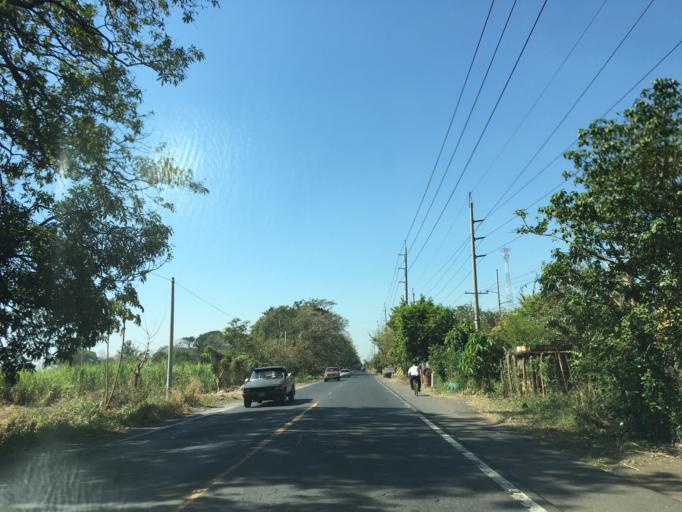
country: GT
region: Escuintla
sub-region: Municipio de Masagua
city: Masagua
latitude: 14.2313
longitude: -90.8238
